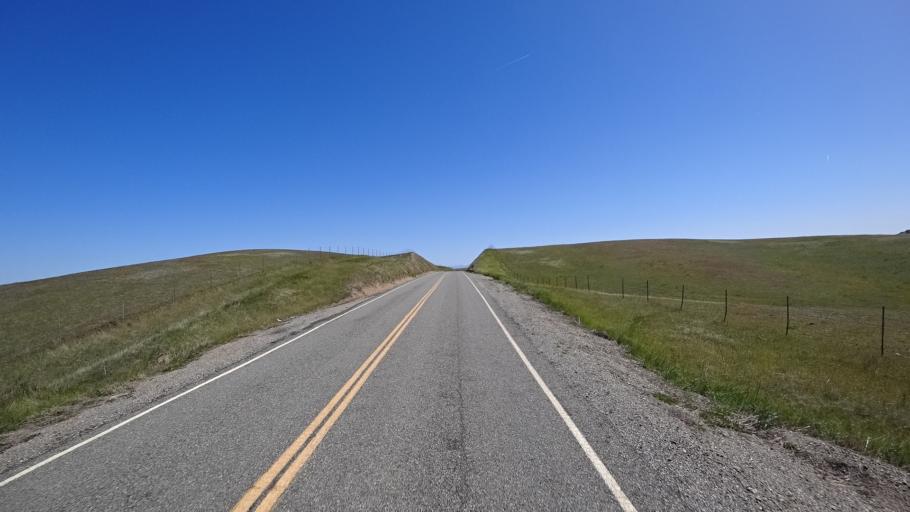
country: US
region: California
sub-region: Tehama County
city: Rancho Tehama Reserve
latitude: 39.8279
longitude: -122.3714
